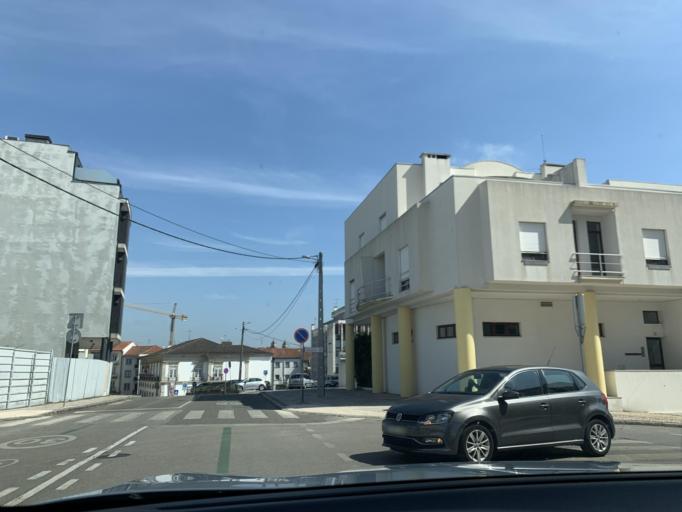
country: PT
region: Viseu
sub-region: Viseu
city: Viseu
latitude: 40.6555
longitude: -7.9117
